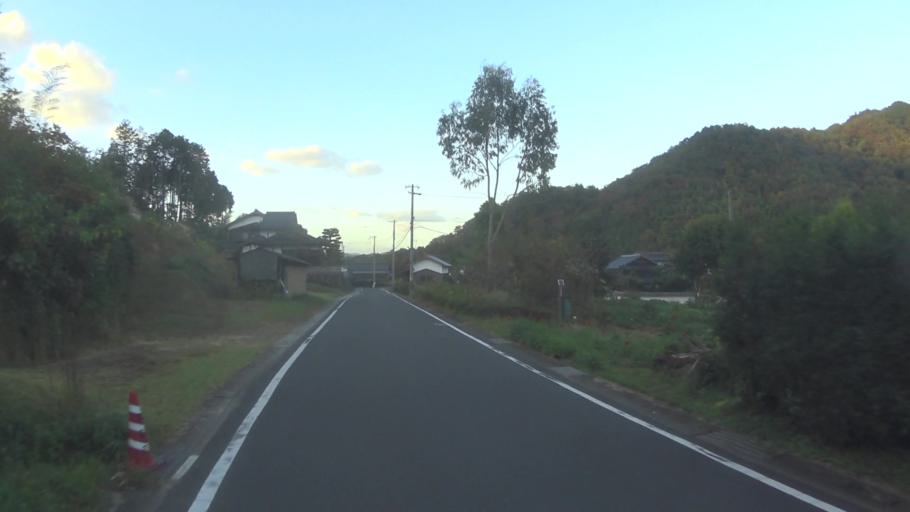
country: JP
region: Kyoto
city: Ayabe
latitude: 35.2895
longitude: 135.2379
